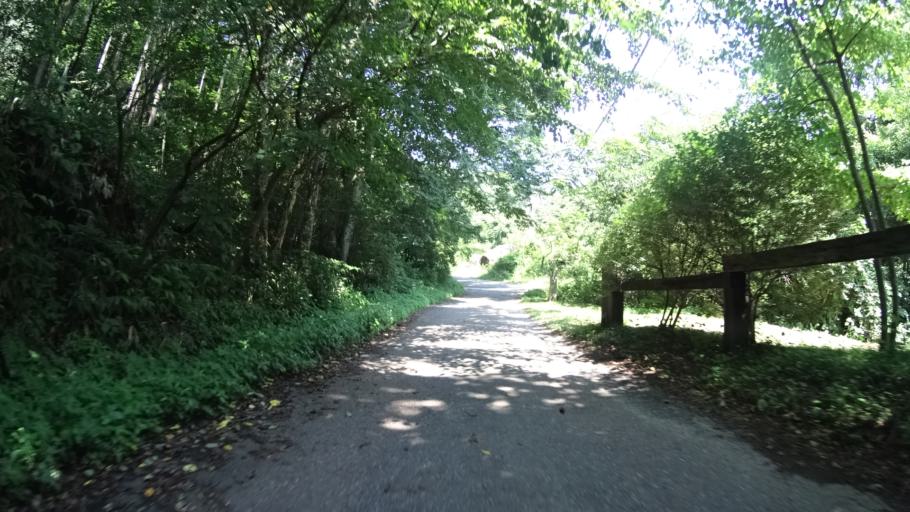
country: JP
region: Yamanashi
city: Nirasaki
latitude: 35.9101
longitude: 138.4206
